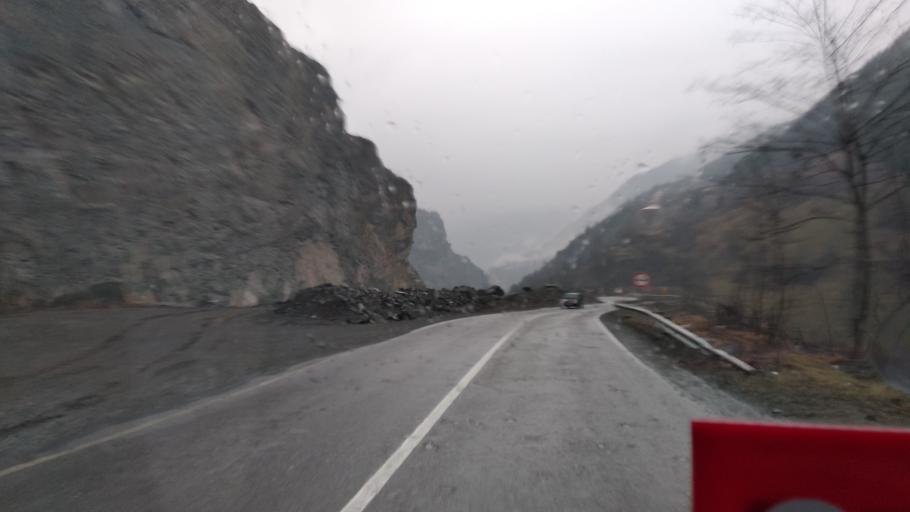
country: TR
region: Trabzon
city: Macka
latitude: 40.7237
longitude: 39.5207
